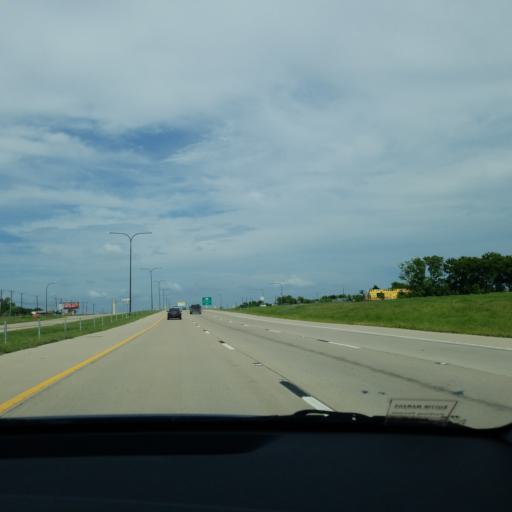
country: US
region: Texas
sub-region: Travis County
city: Manor
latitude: 30.3301
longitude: -97.6317
